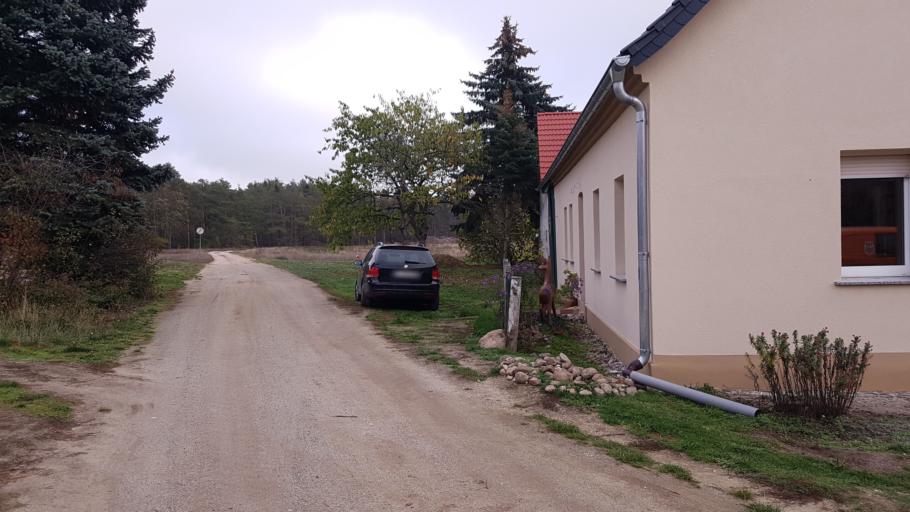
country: DE
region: Brandenburg
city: Schonborn
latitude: 51.6803
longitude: 13.4834
